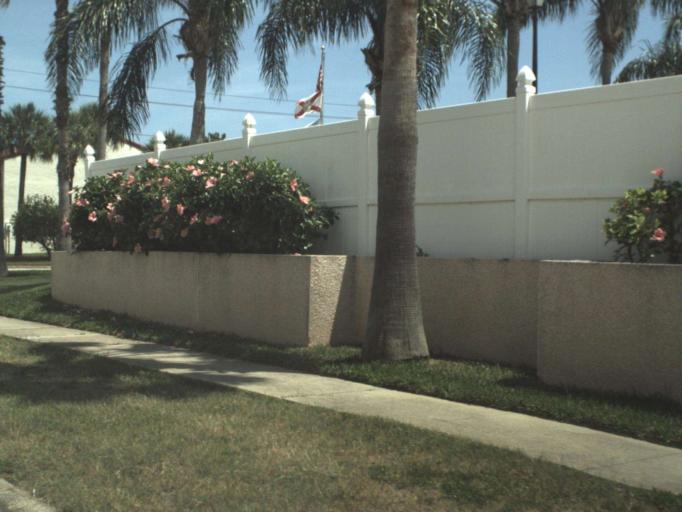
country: US
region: Florida
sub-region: Volusia County
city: Daytona Beach Shores
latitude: 29.1812
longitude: -80.9890
